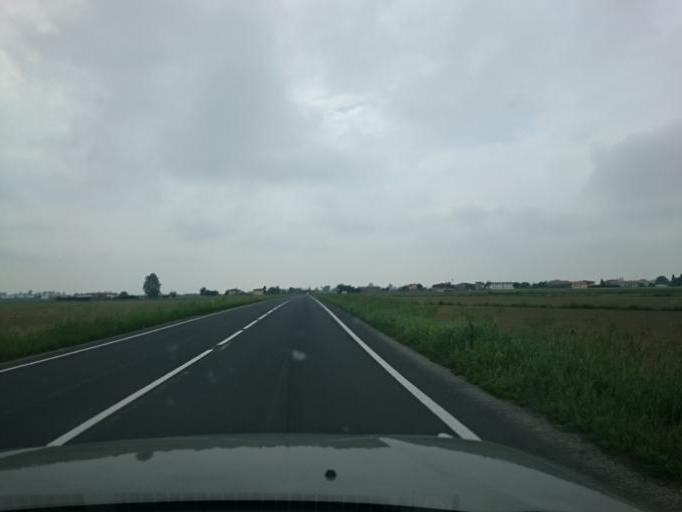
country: IT
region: Veneto
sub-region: Provincia di Padova
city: Codevigo
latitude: 45.2242
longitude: 12.1165
